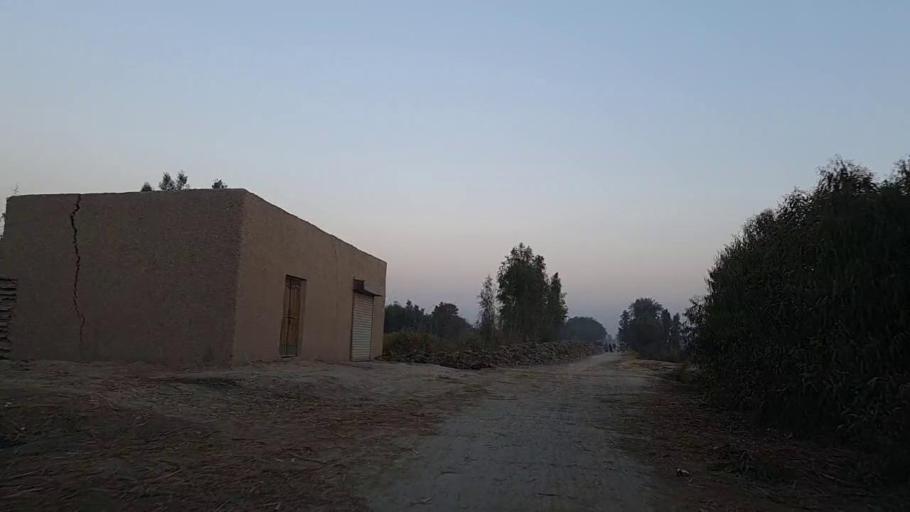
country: PK
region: Sindh
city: Naushahro Firoz
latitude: 26.7983
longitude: 68.0343
